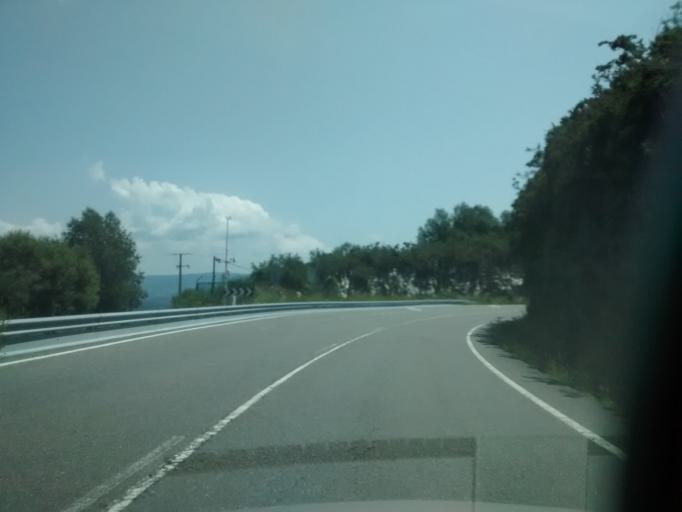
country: ES
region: Galicia
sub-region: Provincia de Ourense
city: Boboras
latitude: 42.4914
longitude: -8.2161
